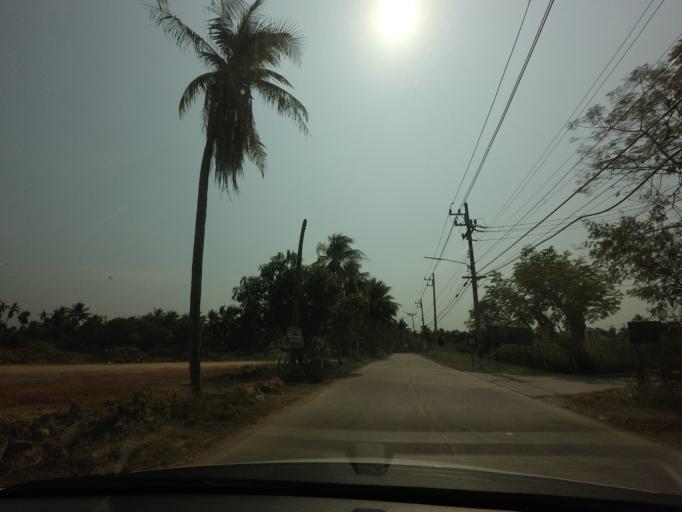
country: TH
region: Nakhon Pathom
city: Sam Phran
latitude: 13.7571
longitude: 100.2599
